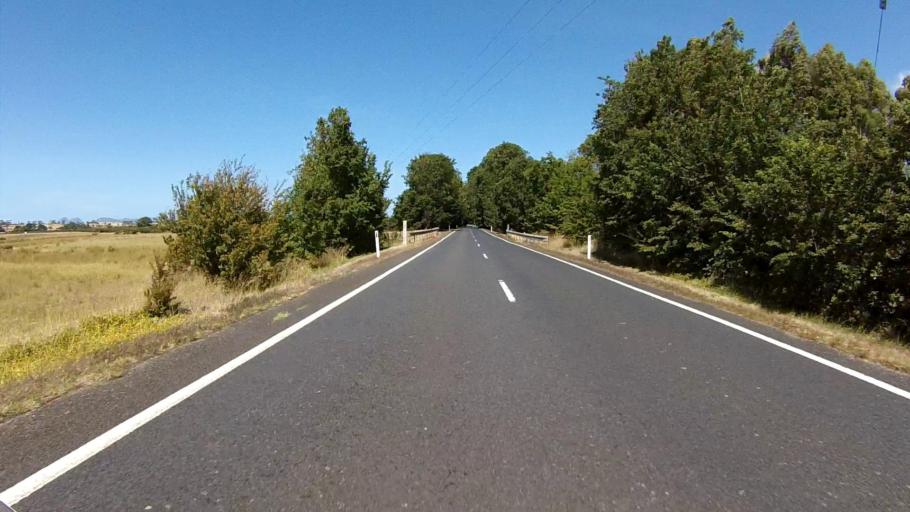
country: AU
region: Tasmania
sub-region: Break O'Day
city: St Helens
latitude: -42.0606
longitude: 148.0616
